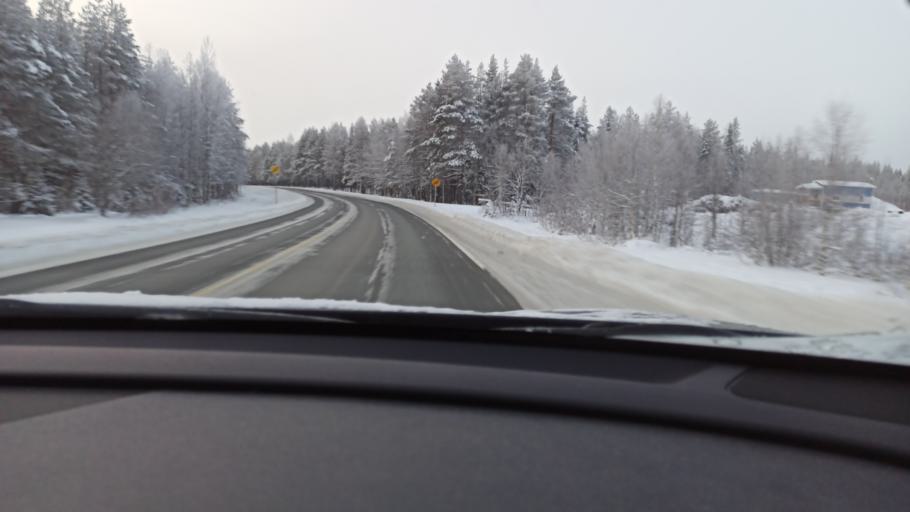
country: FI
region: Lapland
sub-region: Rovaniemi
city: Rovaniemi
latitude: 66.5602
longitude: 25.9091
